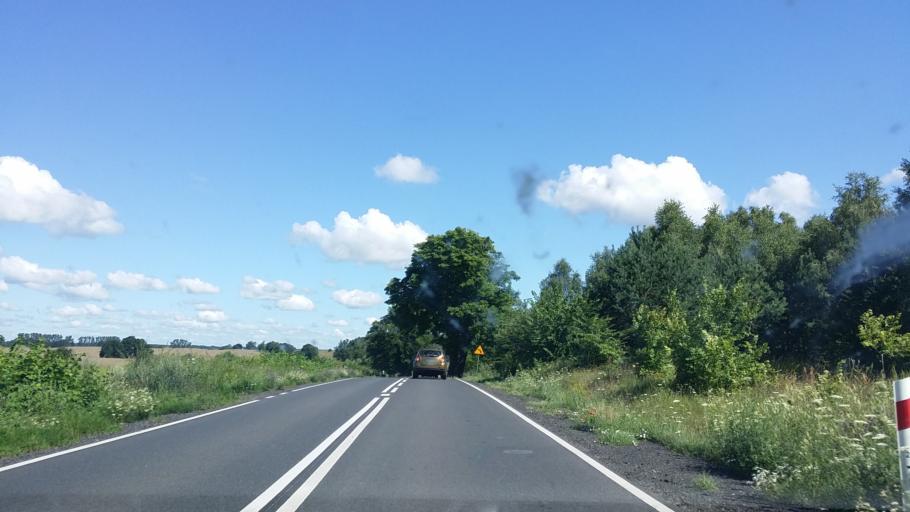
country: PL
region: West Pomeranian Voivodeship
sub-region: Powiat drawski
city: Kalisz Pomorski
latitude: 53.3090
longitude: 15.9087
